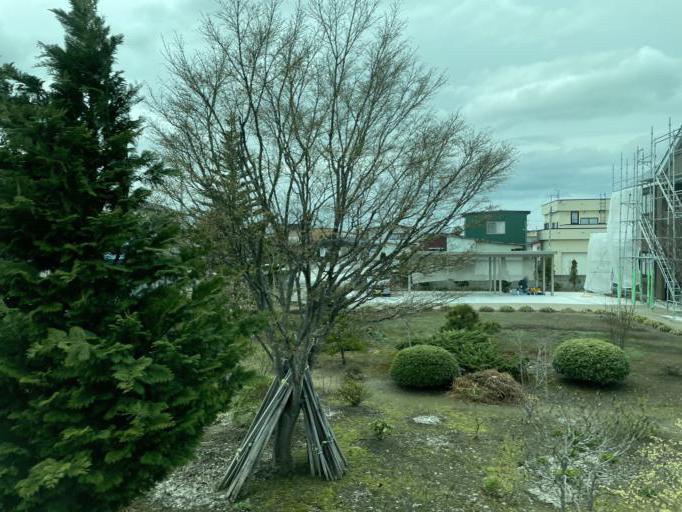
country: JP
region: Aomori
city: Goshogawara
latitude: 40.7541
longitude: 140.4347
